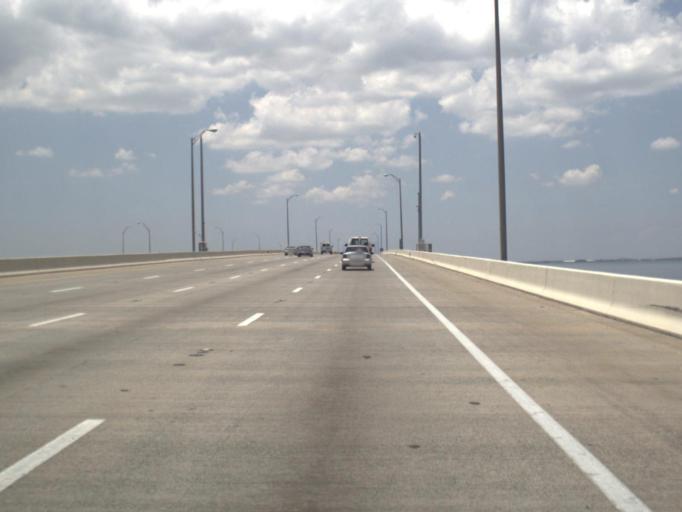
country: US
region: Florida
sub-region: Pinellas County
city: Gandy
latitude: 27.9298
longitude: -82.5831
